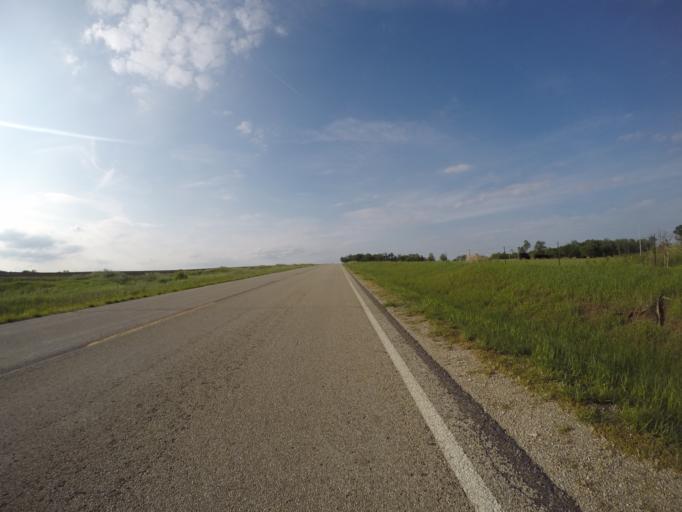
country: US
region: Kansas
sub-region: Pottawatomie County
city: Westmoreland
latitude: 39.4234
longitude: -96.6069
